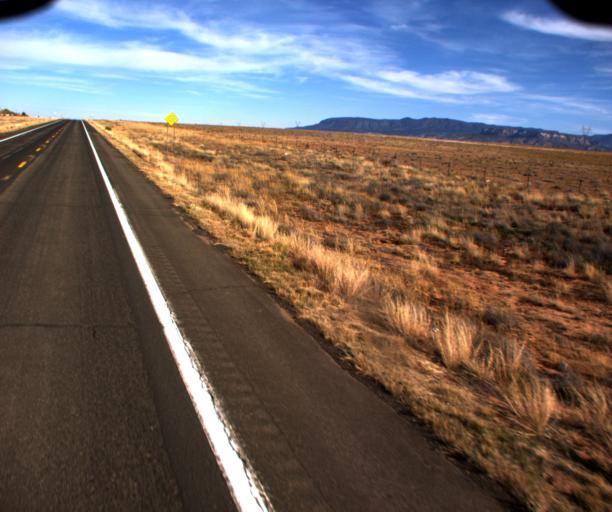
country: US
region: Arizona
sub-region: Apache County
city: Lukachukai
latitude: 36.9612
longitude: -109.3928
